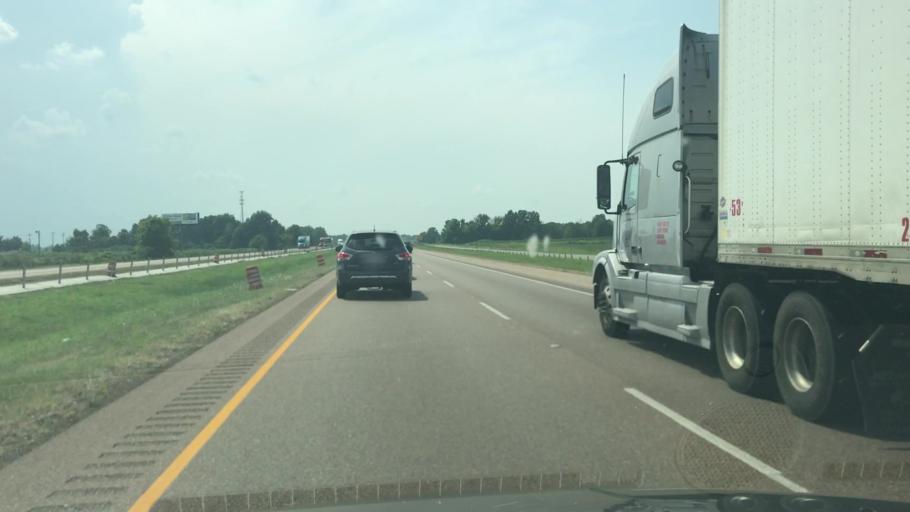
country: US
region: Arkansas
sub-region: Crittenden County
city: West Memphis
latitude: 35.1493
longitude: -90.3501
